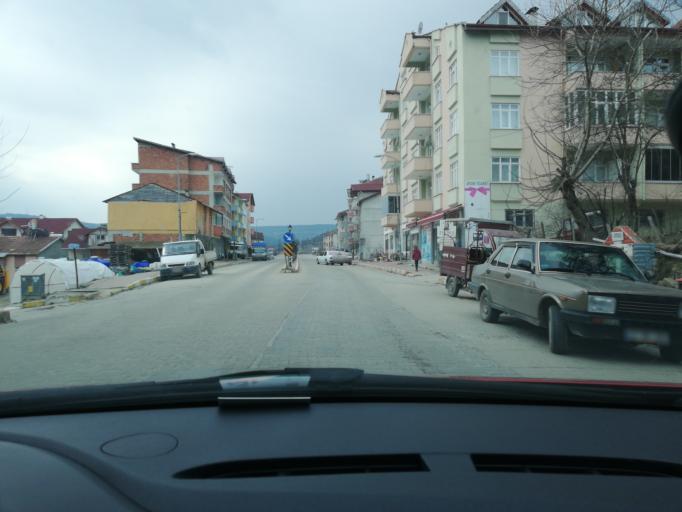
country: TR
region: Kastamonu
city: Pinarbasi
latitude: 41.6033
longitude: 33.1097
